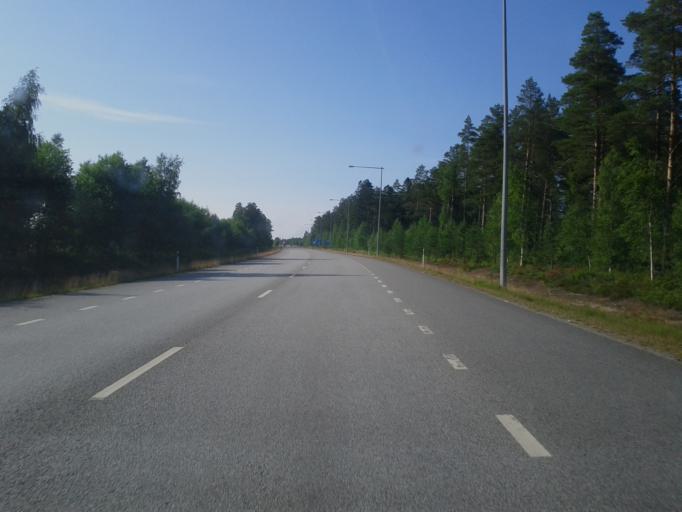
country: SE
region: Vaesterbotten
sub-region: Umea Kommun
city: Umea
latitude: 63.7926
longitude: 20.2959
